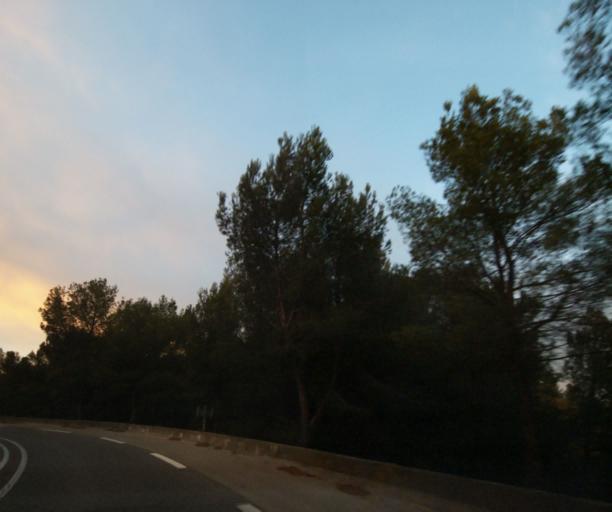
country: FR
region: Provence-Alpes-Cote d'Azur
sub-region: Departement des Bouches-du-Rhone
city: Sausset-les-Pins
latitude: 43.3360
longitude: 5.0893
